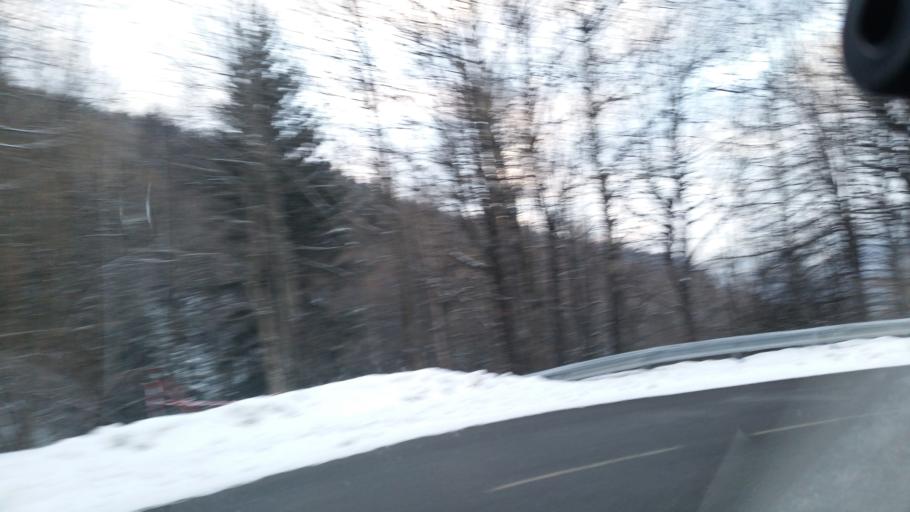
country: FR
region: Rhone-Alpes
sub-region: Departement de la Savoie
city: Villargondran
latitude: 45.2347
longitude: 6.4097
